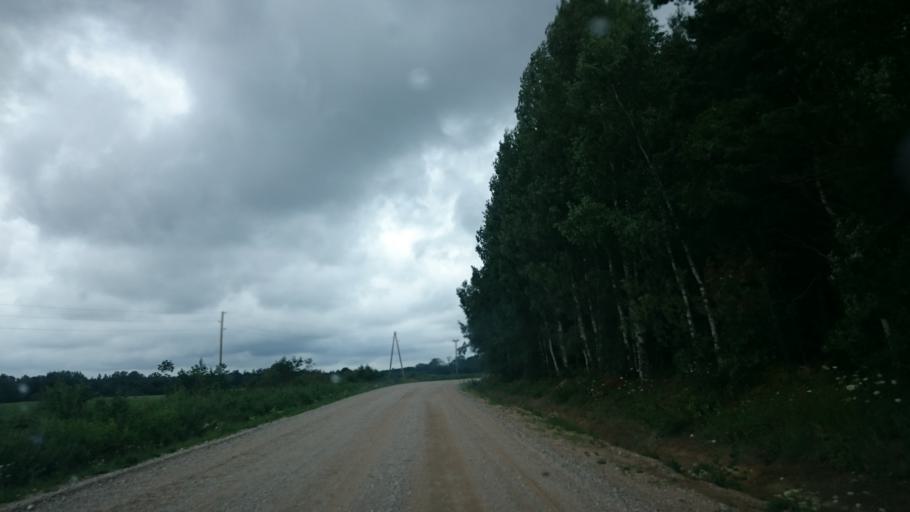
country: LV
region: Pavilostas
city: Pavilosta
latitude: 56.8522
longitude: 21.2515
